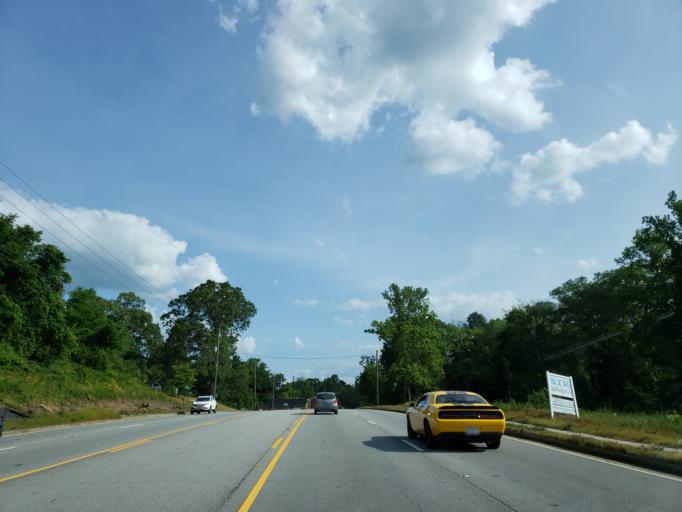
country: US
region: Georgia
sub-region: Carroll County
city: Carrollton
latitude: 33.5865
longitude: -85.0785
